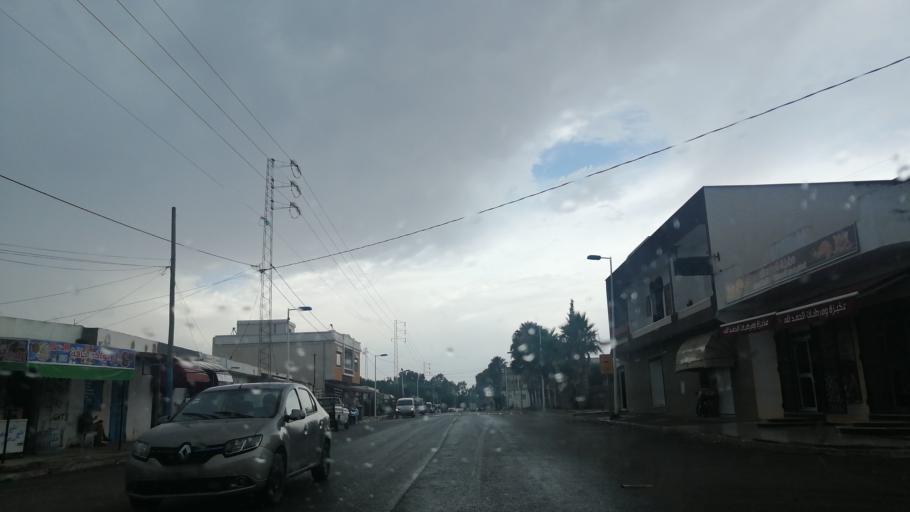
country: TN
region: Al Qayrawan
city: Sbikha
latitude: 36.1230
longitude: 10.0915
